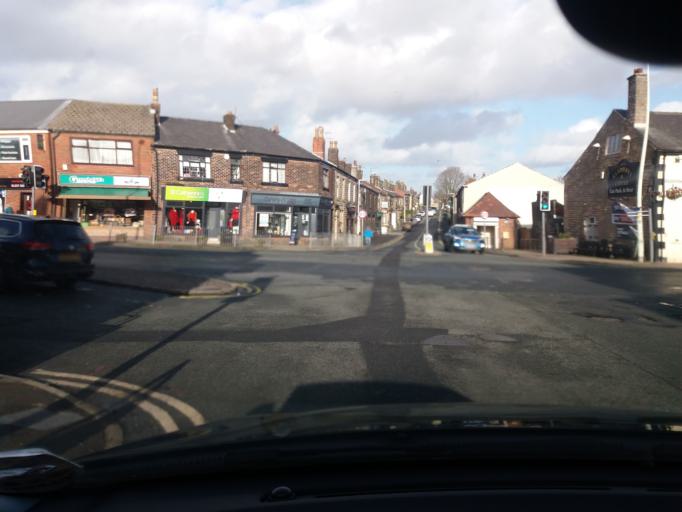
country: GB
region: England
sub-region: Lancashire
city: Adlington
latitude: 53.6172
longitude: -2.5975
